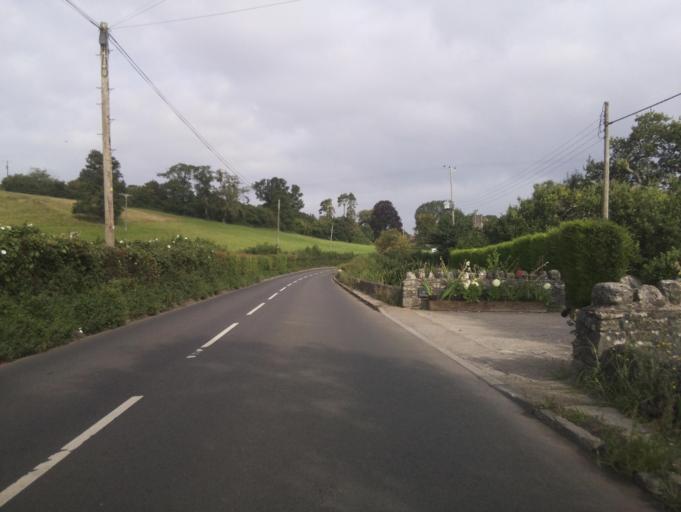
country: GB
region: England
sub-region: North Somerset
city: Long Ashton
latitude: 51.4133
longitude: -2.6862
